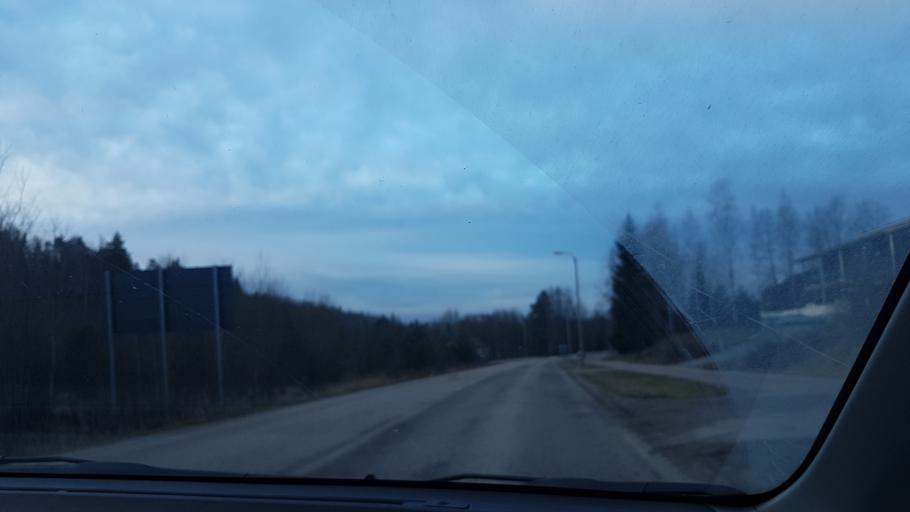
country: FI
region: Uusimaa
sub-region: Helsinki
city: Nurmijaervi
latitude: 60.3722
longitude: 24.7589
